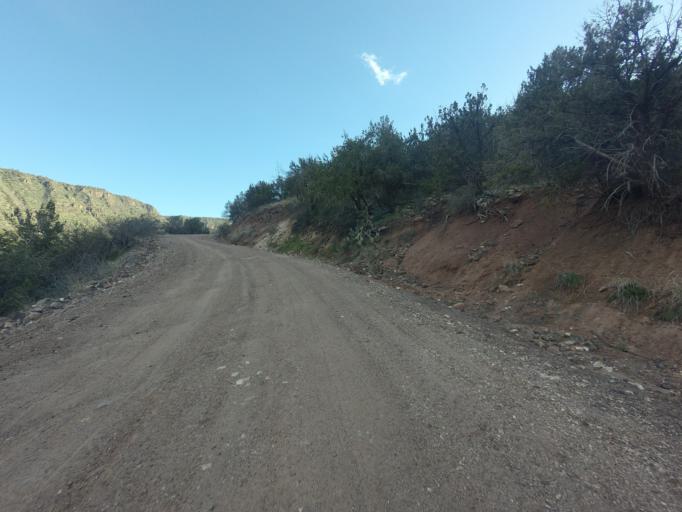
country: US
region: Arizona
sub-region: Gila County
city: Pine
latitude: 34.3782
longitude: -111.6605
